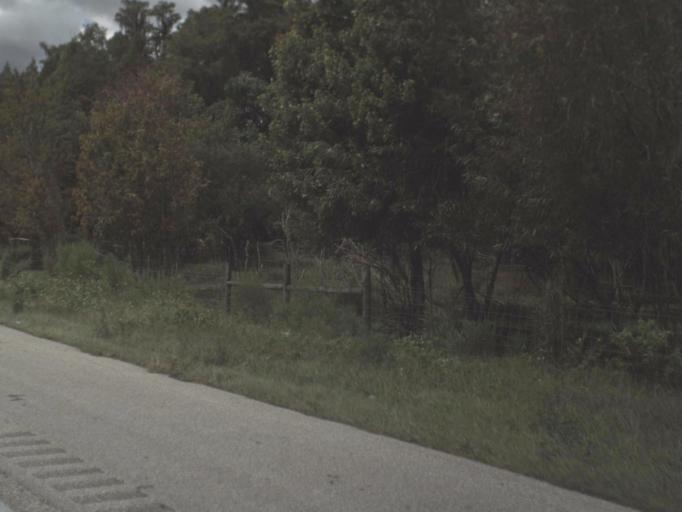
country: US
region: Florida
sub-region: Polk County
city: Davenport
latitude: 28.2246
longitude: -81.6610
